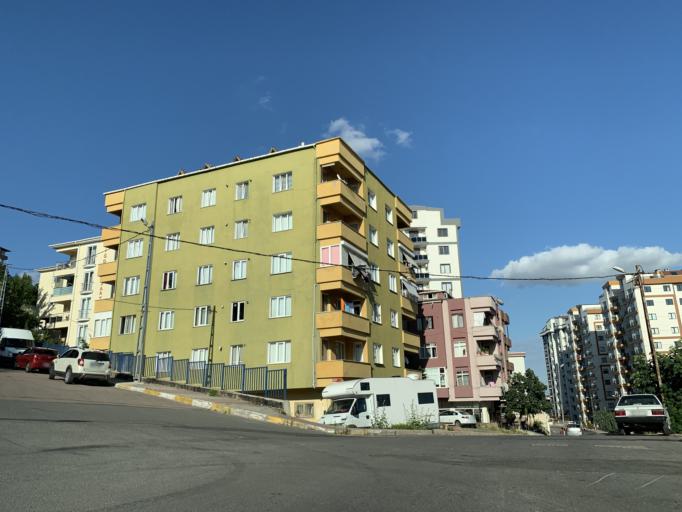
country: TR
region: Istanbul
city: Pendik
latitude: 40.8971
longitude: 29.2455
